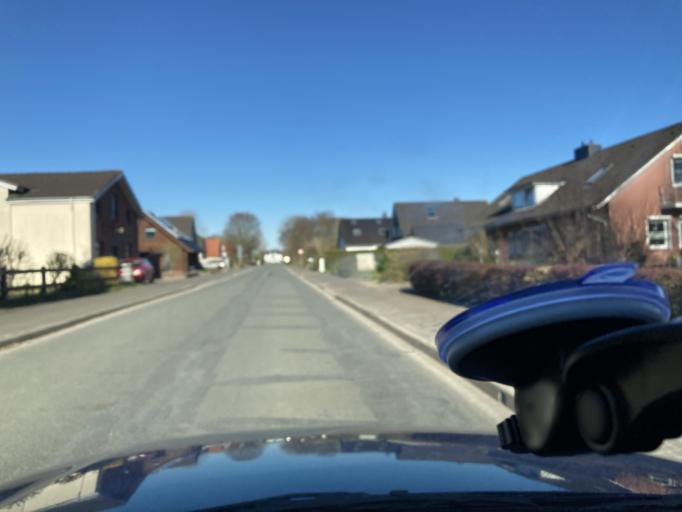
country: DE
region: Schleswig-Holstein
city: Neuenkirchen
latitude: 54.2368
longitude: 8.9971
